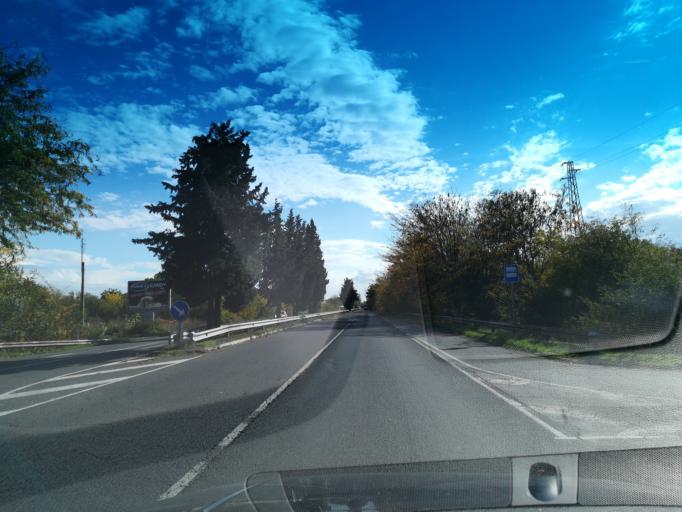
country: BG
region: Stara Zagora
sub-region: Obshtina Stara Zagora
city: Stara Zagora
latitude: 42.3885
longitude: 25.6477
